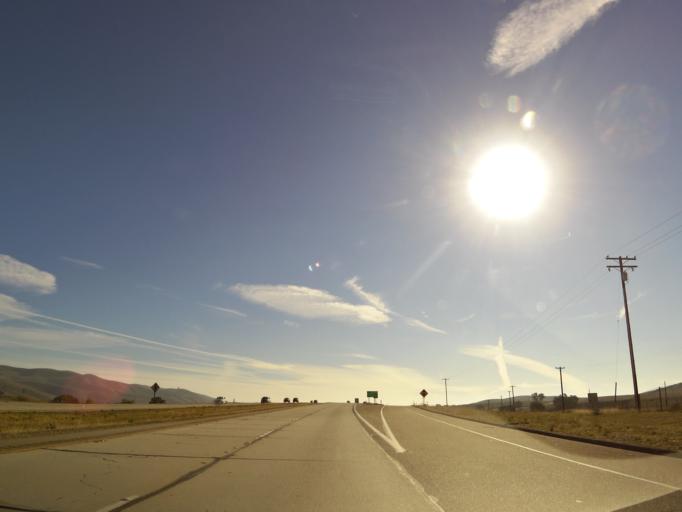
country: US
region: California
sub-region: San Luis Obispo County
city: San Miguel
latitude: 35.7777
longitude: -120.7164
